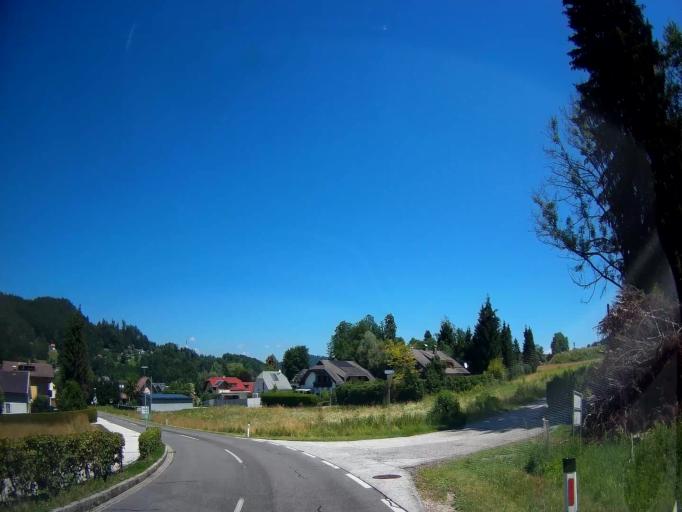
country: AT
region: Carinthia
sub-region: Politischer Bezirk Klagenfurt Land
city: Keutschach am See
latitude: 46.5988
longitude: 14.1745
